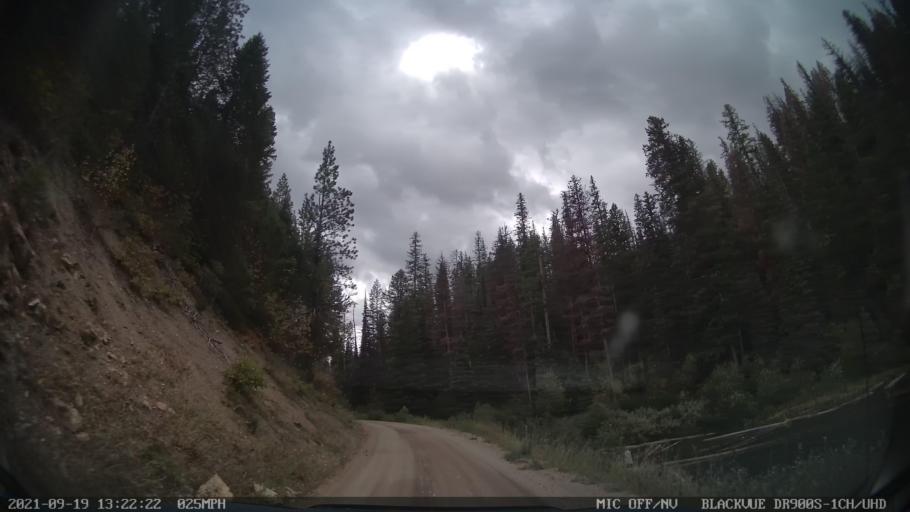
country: US
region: Montana
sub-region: Missoula County
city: Seeley Lake
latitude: 47.1645
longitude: -113.3490
